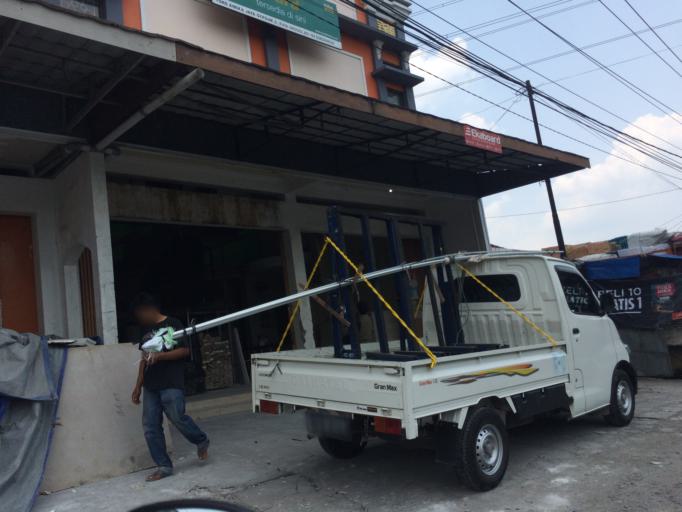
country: ID
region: Central Java
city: Grogol
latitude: -7.6100
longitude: 110.8188
